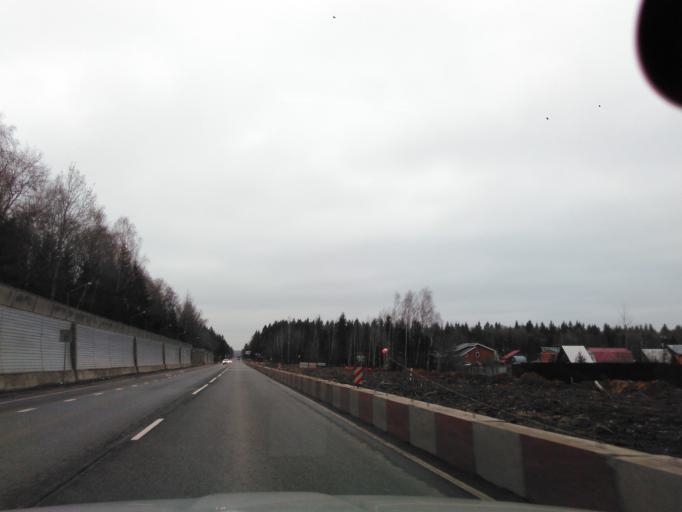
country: RU
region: Moskovskaya
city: Snegiri
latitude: 55.9508
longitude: 36.9736
